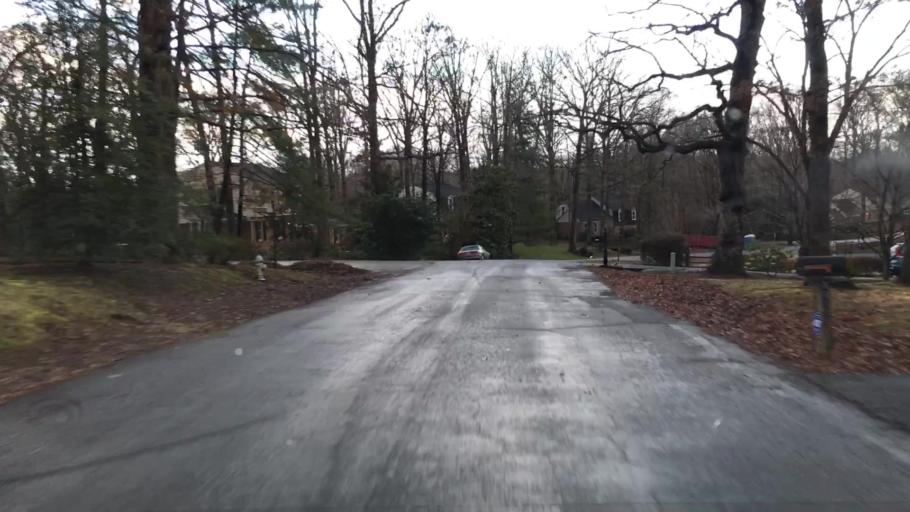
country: US
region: Virginia
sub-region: Chesterfield County
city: Bon Air
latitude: 37.5163
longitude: -77.6266
